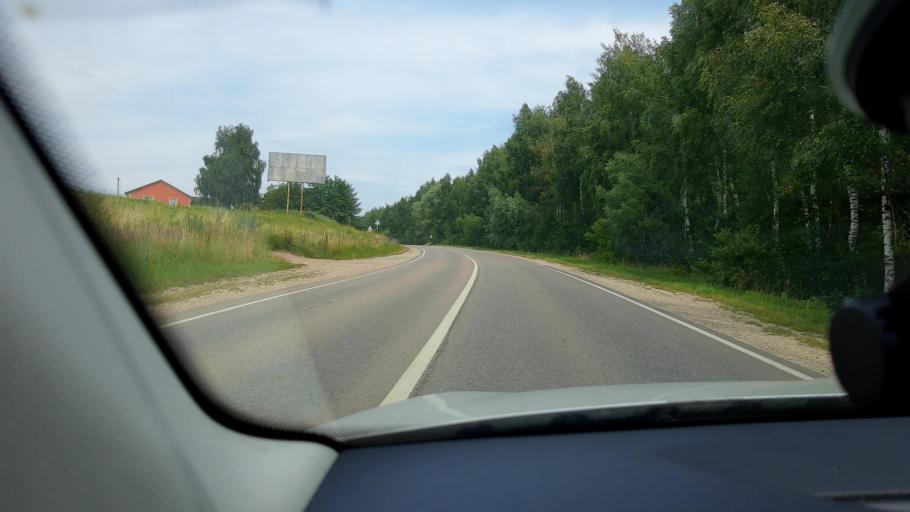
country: RU
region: Moskovskaya
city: Serpukhov
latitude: 54.8238
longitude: 37.4530
